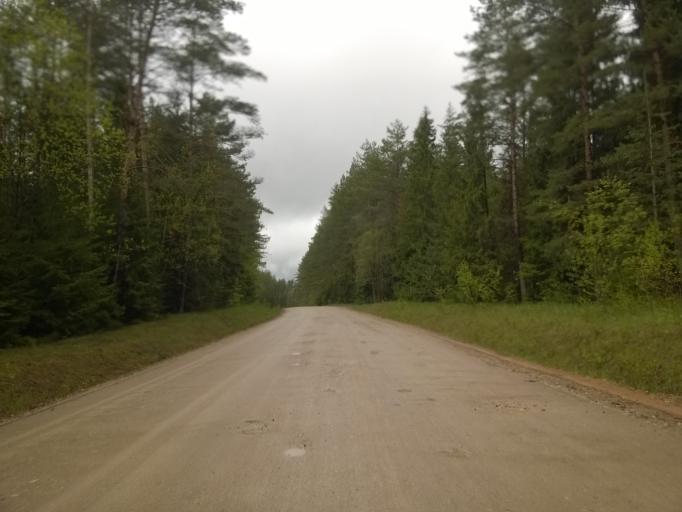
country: LV
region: Amatas Novads
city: Drabesi
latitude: 57.2129
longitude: 25.2340
